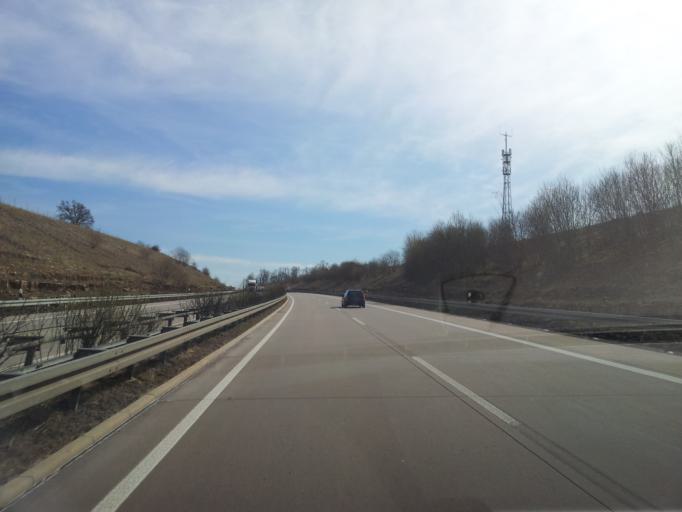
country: DE
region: Thuringia
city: Wolfershausen
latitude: 50.4881
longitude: 10.4418
